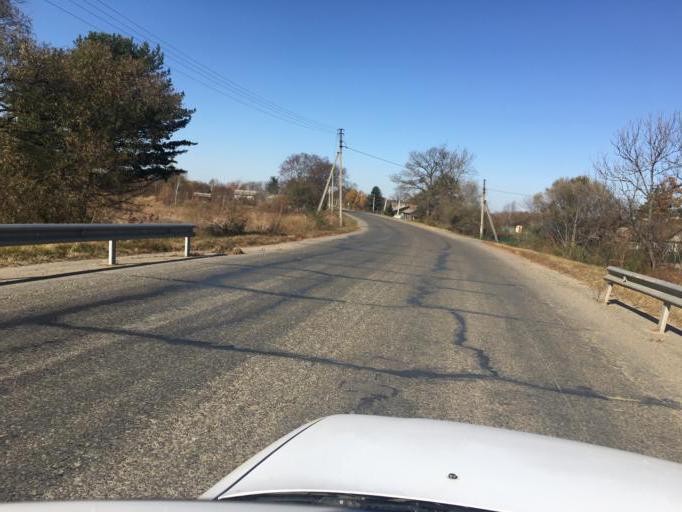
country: RU
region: Primorskiy
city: Dal'nerechensk
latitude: 45.9144
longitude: 133.7891
